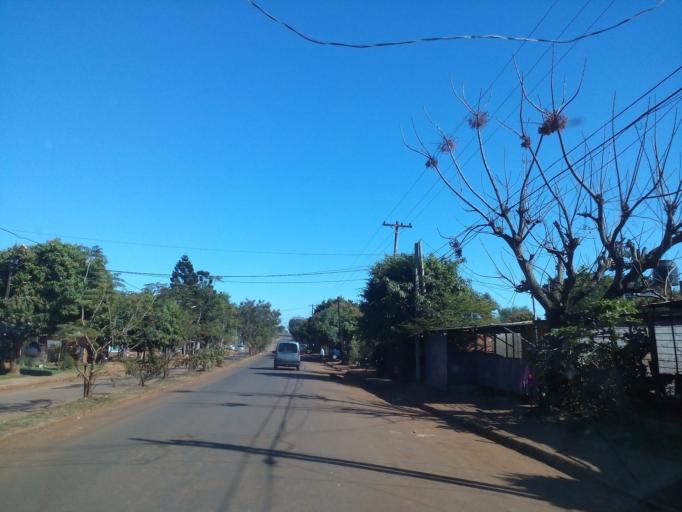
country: AR
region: Misiones
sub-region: Departamento de Capital
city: Posadas
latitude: -27.3892
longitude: -55.9231
